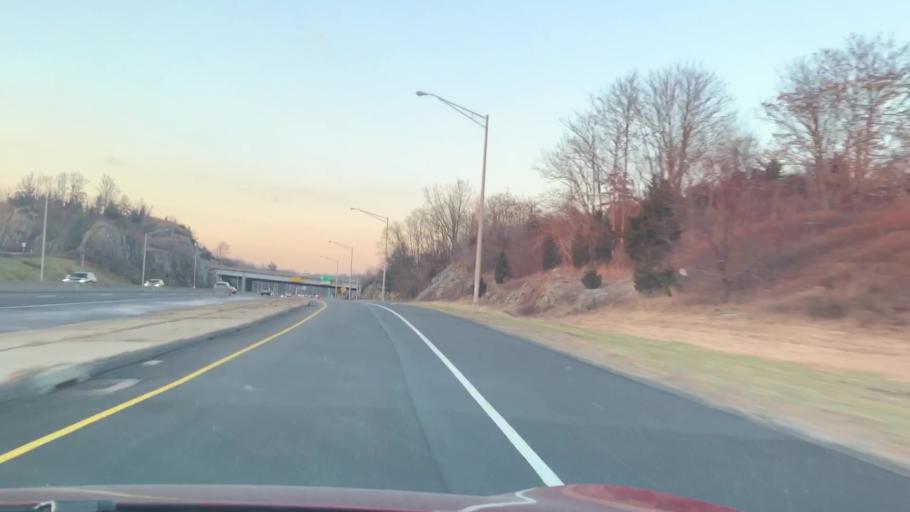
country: US
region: Connecticut
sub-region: Fairfield County
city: Norwalk
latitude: 41.1384
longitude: -73.4300
